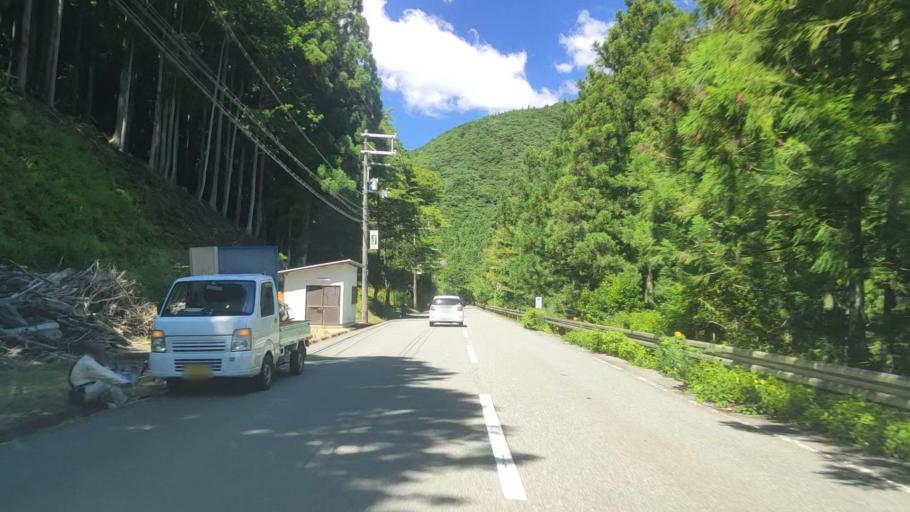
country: JP
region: Mie
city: Owase
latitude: 34.1709
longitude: 136.0016
